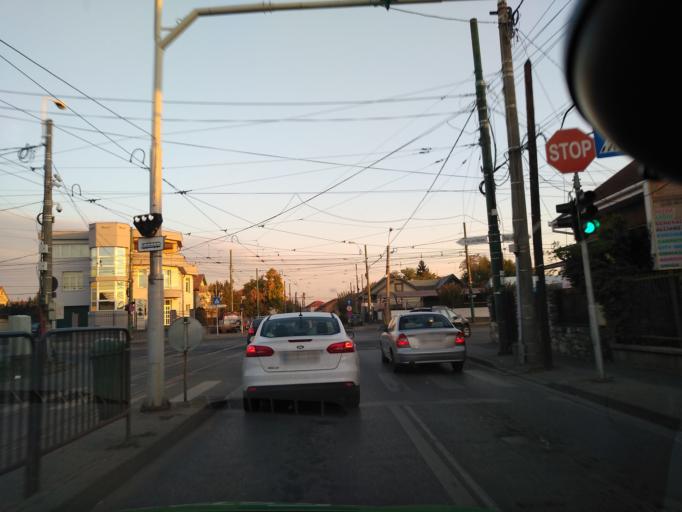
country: RO
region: Timis
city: Timisoara
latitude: 45.7348
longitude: 21.2268
